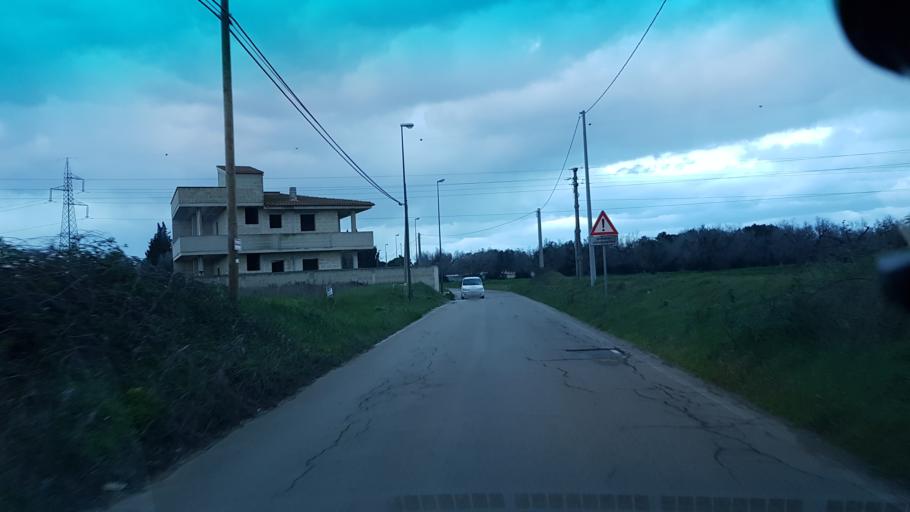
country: IT
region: Apulia
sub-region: Provincia di Brindisi
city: Torchiarolo
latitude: 40.4907
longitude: 18.0534
